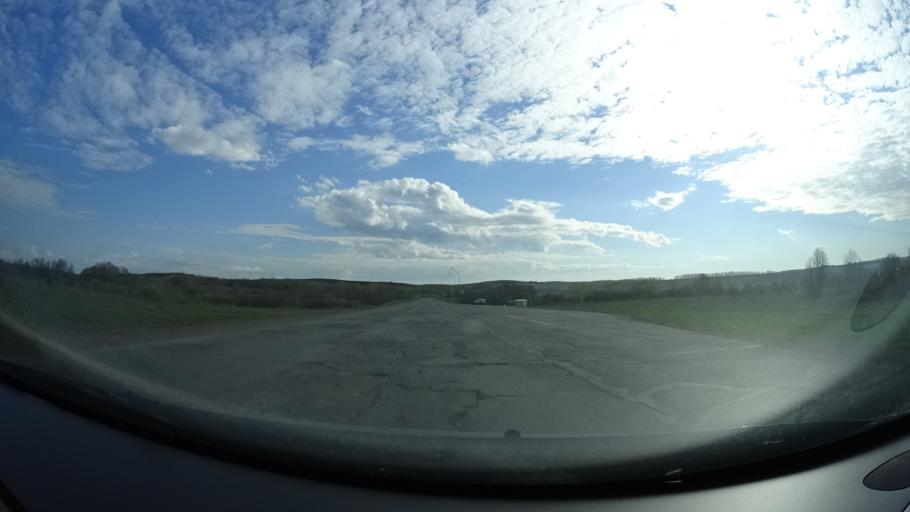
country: RU
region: Bashkortostan
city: Blagoveshchensk
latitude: 55.1079
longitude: 55.8336
